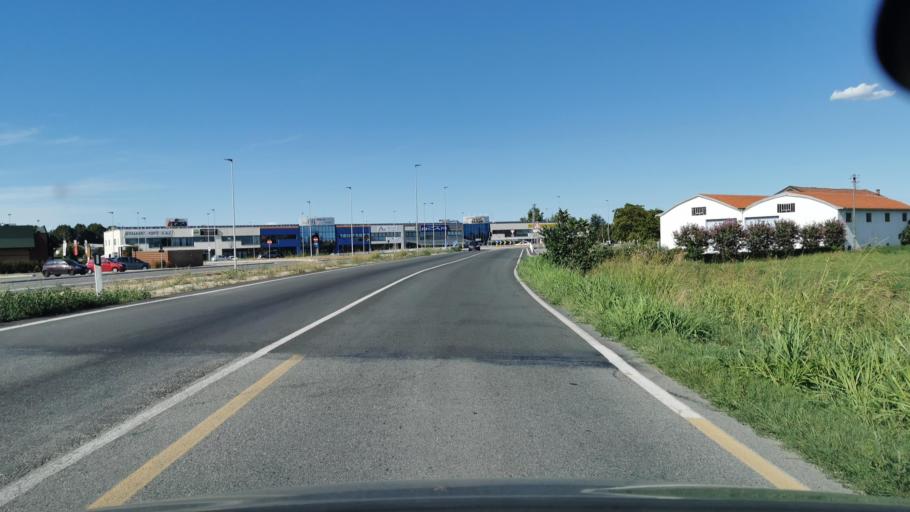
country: IT
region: Piedmont
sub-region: Provincia di Cuneo
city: Savigliano
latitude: 44.6474
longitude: 7.6754
